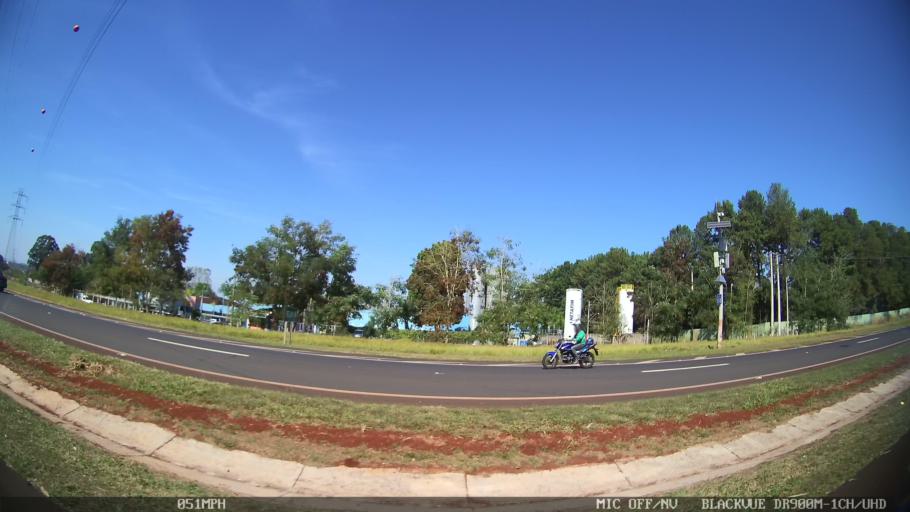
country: BR
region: Sao Paulo
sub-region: Ribeirao Preto
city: Ribeirao Preto
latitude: -21.1198
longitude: -47.8323
